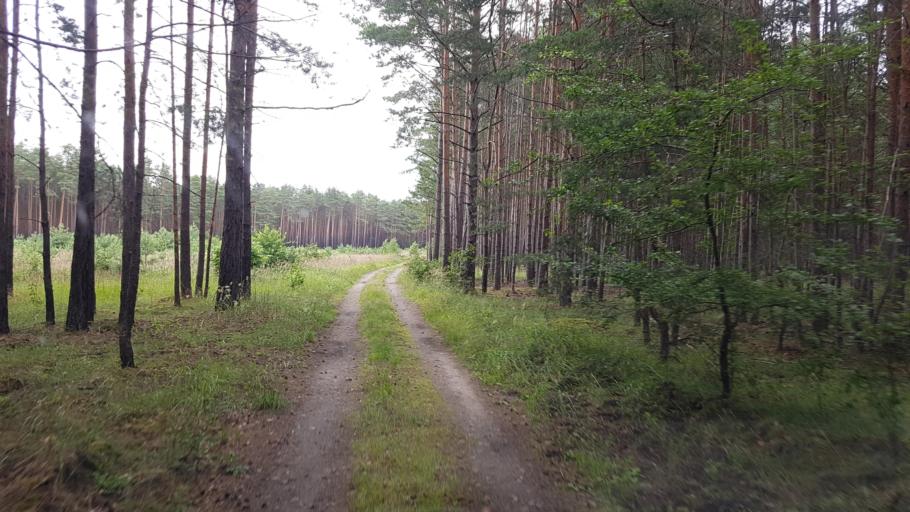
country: DE
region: Brandenburg
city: Grossraschen
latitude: 51.6009
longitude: 14.0372
